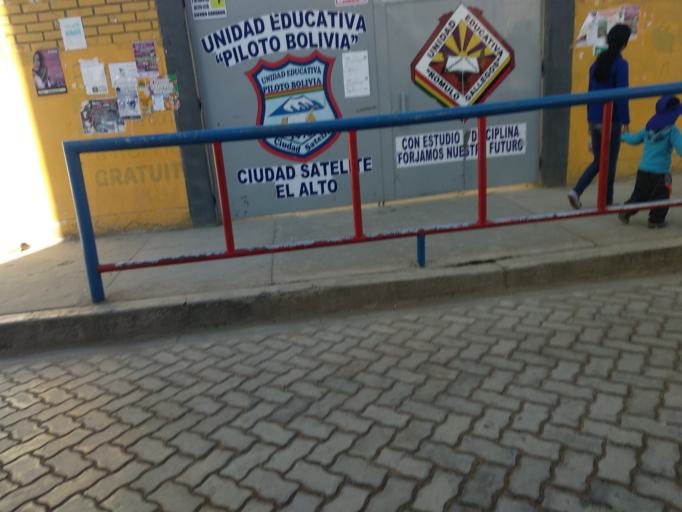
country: BO
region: La Paz
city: La Paz
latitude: -16.5263
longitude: -68.1542
